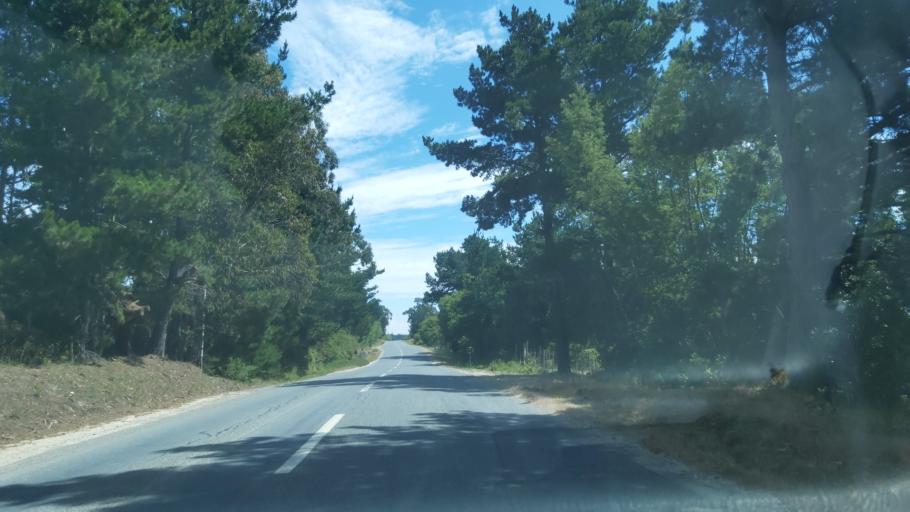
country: CL
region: Maule
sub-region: Provincia de Talca
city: Constitucion
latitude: -35.5618
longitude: -72.5902
